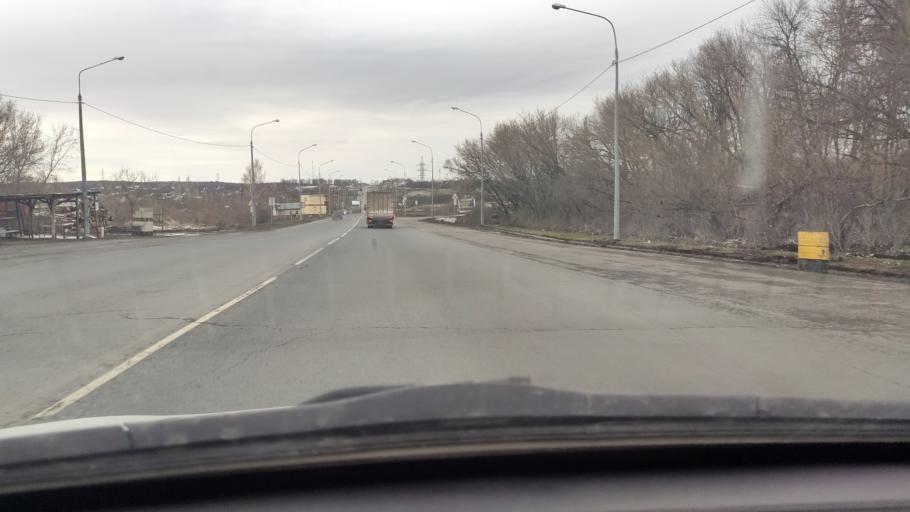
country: RU
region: Samara
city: Zhigulevsk
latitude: 53.3628
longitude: 49.4579
